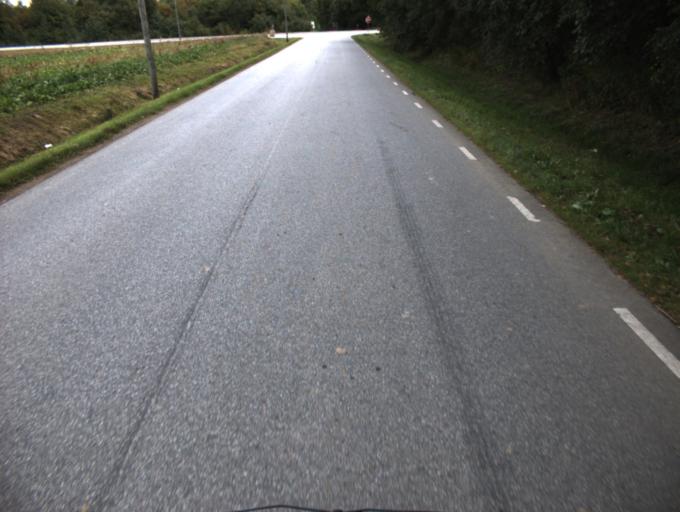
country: SE
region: Skane
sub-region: Helsingborg
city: Odakra
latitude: 56.0807
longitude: 12.7629
